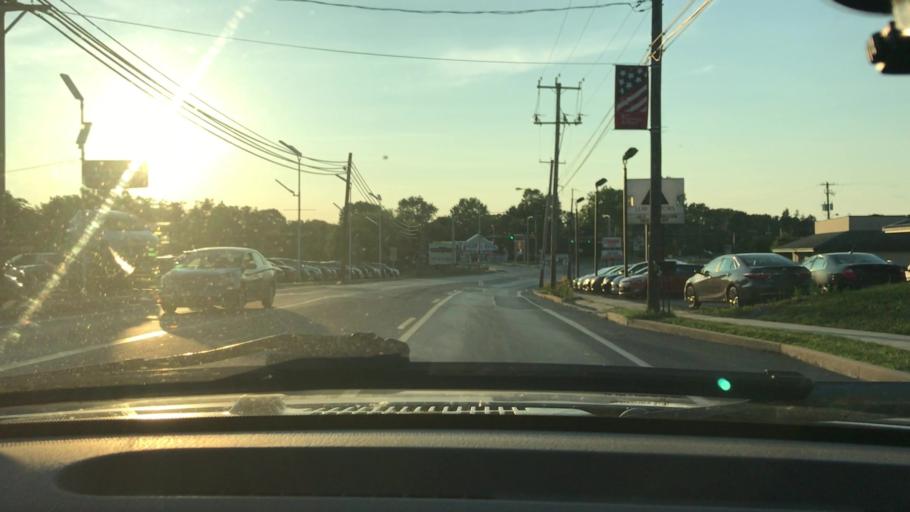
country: US
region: Pennsylvania
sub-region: Lancaster County
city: East Petersburg
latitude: 40.0926
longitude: -76.3493
